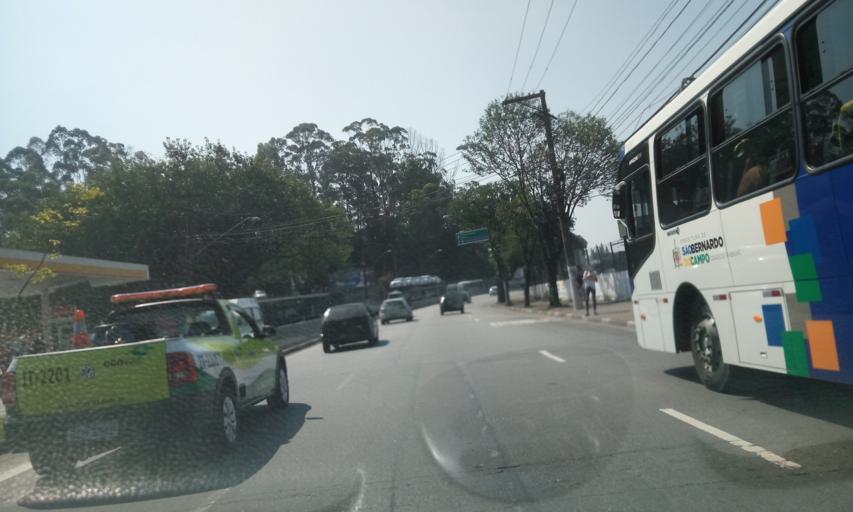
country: BR
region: Sao Paulo
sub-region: Sao Bernardo Do Campo
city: Sao Bernardo do Campo
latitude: -23.7318
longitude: -46.5522
